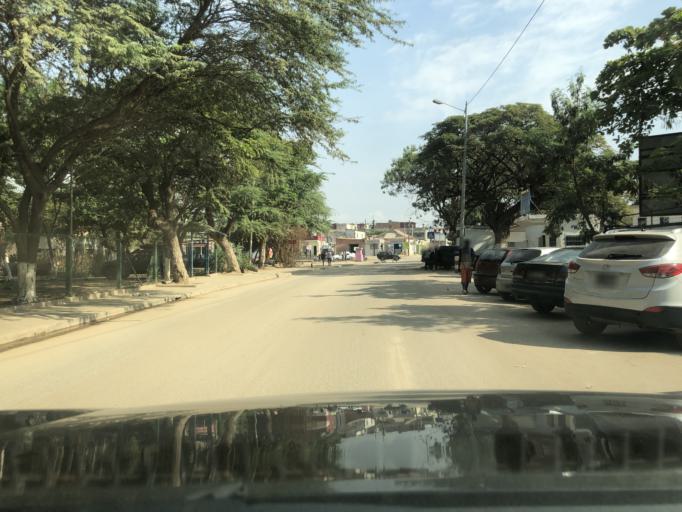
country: AO
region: Luanda
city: Luanda
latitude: -8.8474
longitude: 13.2598
